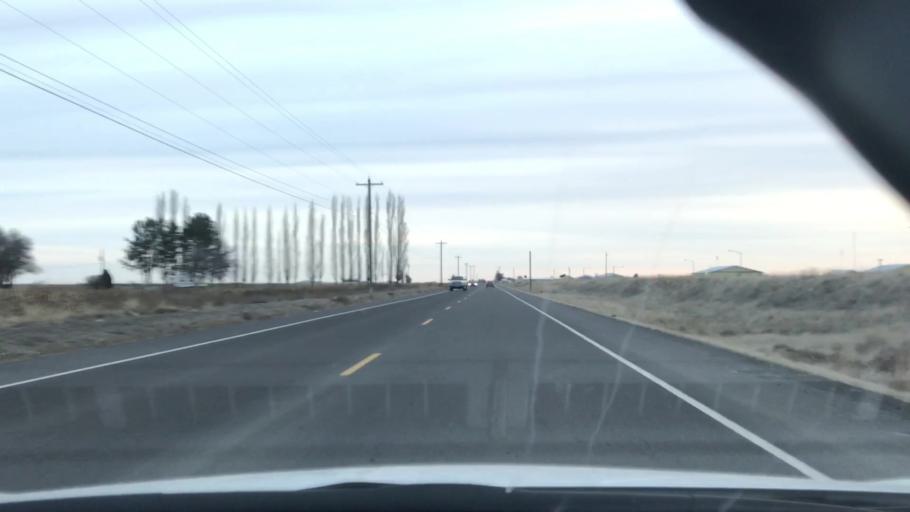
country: US
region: Washington
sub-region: Grant County
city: Moses Lake
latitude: 47.1453
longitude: -119.2356
